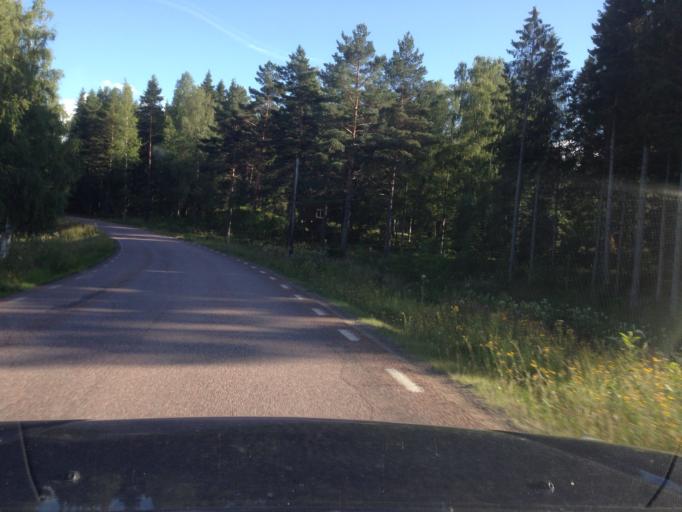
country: SE
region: Dalarna
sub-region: Ludvika Kommun
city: Grangesberg
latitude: 60.1861
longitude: 14.9693
